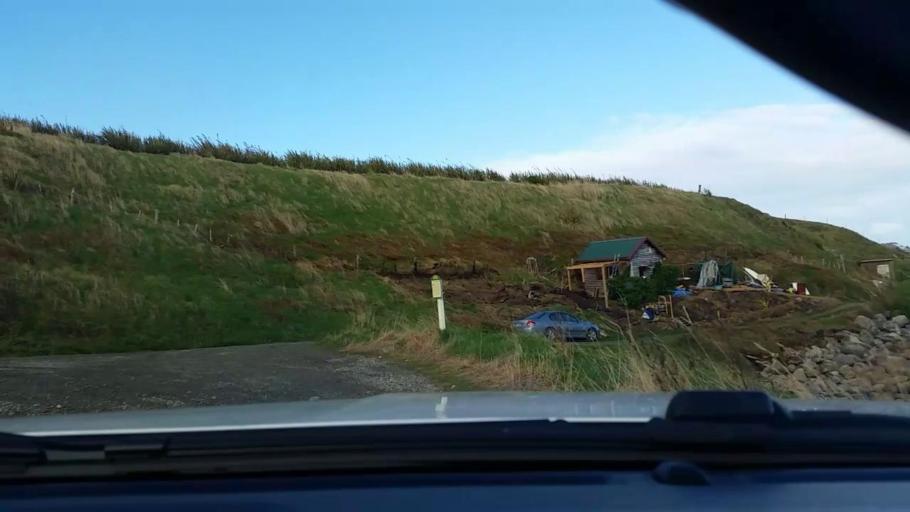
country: NZ
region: Southland
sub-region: Southland District
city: Riverton
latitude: -46.3315
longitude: 167.7125
